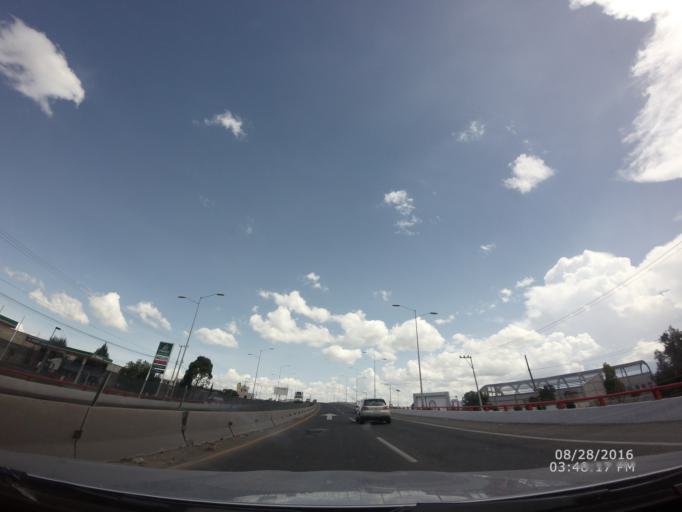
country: MX
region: Hidalgo
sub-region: Mineral de la Reforma
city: Nuevo Centro de Poblacion Agricola el Chacon
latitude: 20.0577
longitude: -98.7429
